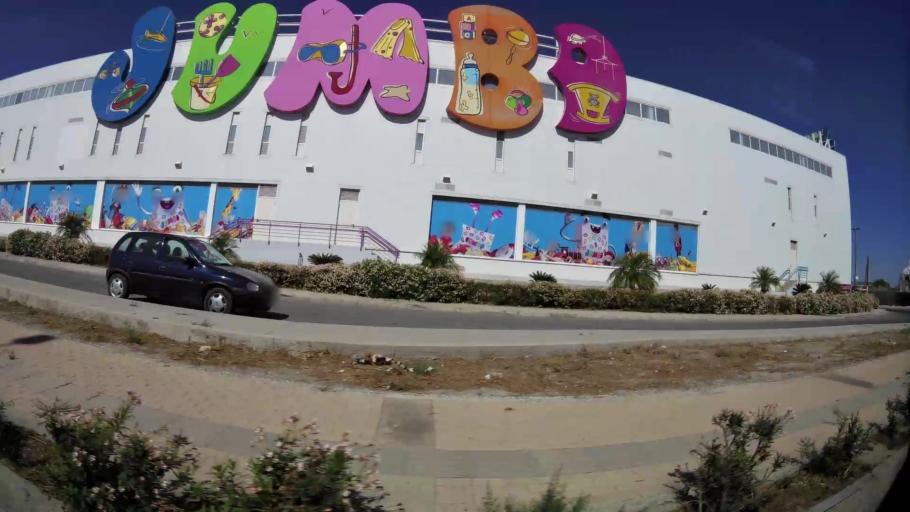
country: CY
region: Larnaka
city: Livadia
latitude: 34.9488
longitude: 33.6465
